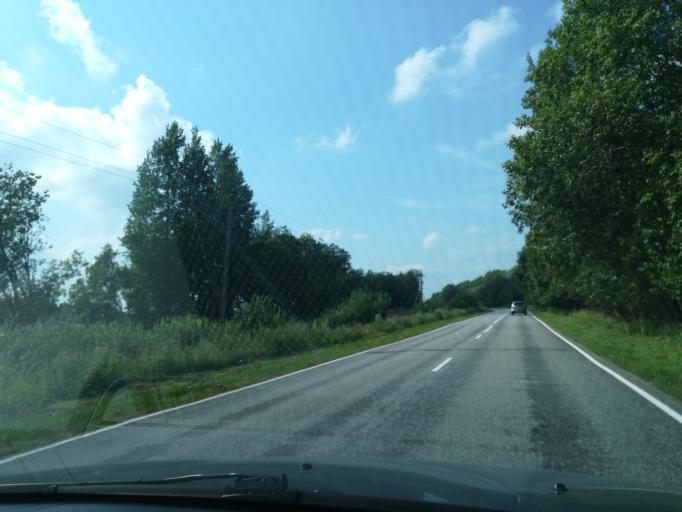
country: RU
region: Leningrad
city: Kopor'ye
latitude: 59.7299
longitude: 29.1171
